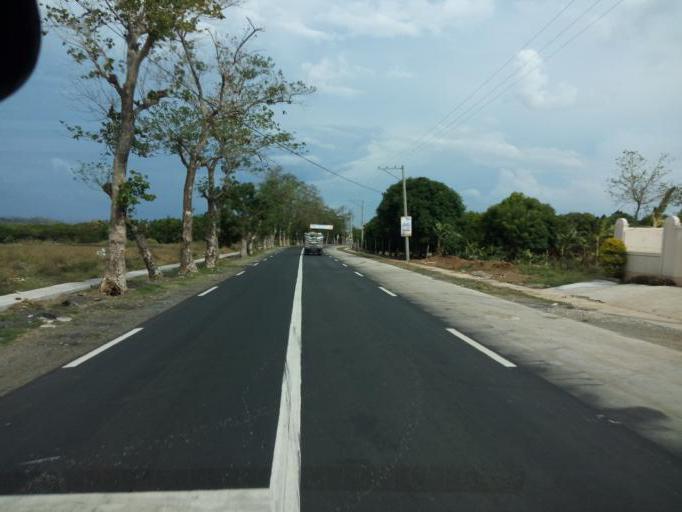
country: PH
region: Central Luzon
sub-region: Province of Nueva Ecija
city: Parista
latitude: 15.8252
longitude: 120.9514
